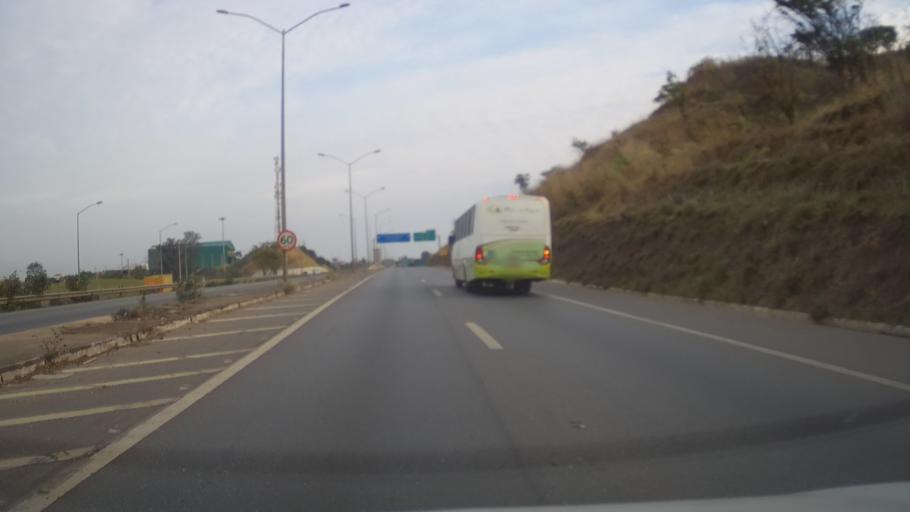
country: BR
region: Minas Gerais
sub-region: Vespasiano
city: Vespasiano
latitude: -19.7629
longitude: -43.9480
